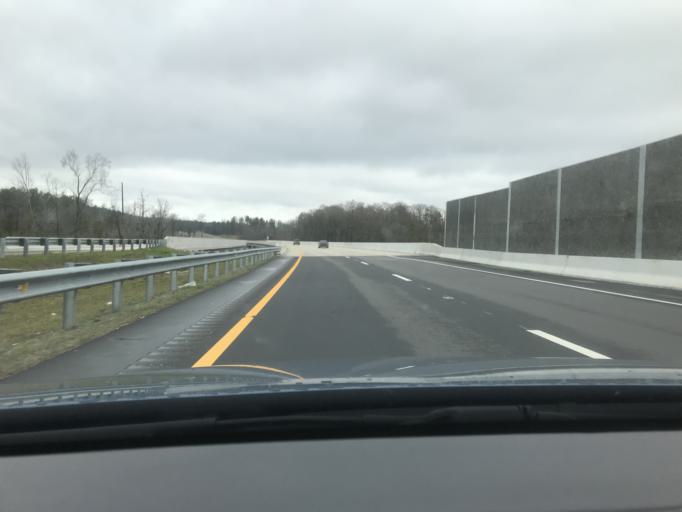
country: US
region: North Carolina
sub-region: Cumberland County
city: Fort Bragg
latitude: 35.0786
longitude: -79.0205
